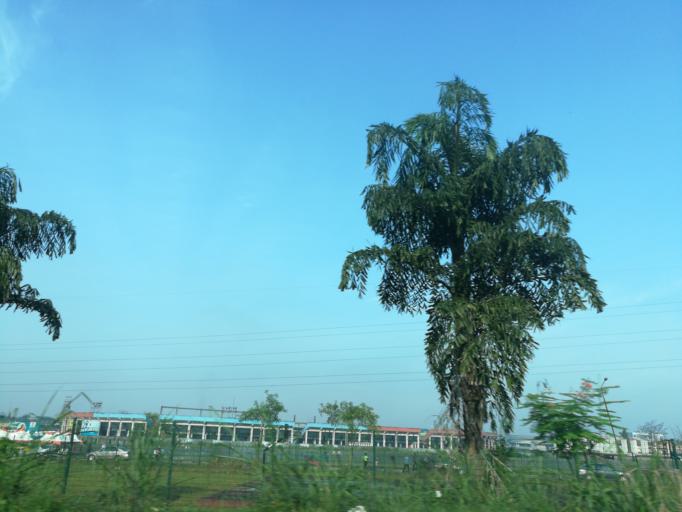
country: NG
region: Rivers
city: Port Harcourt
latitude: 4.8246
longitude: 7.0246
